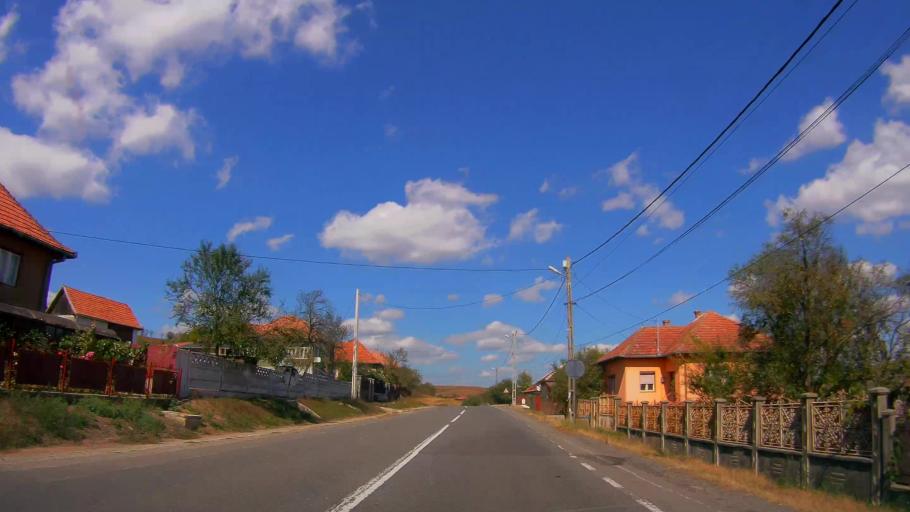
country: RO
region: Cluj
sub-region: Comuna Sanpaul
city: Sanpaul
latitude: 46.9086
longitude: 23.4169
